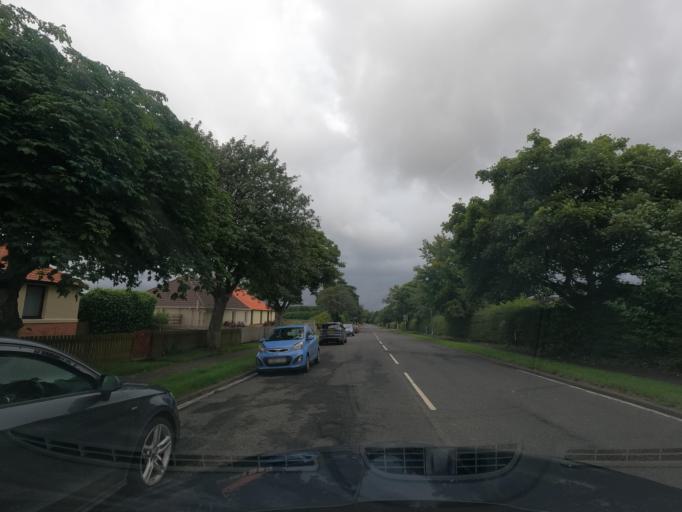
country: GB
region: England
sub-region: Northumberland
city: Ancroft
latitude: 55.7377
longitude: -1.9920
